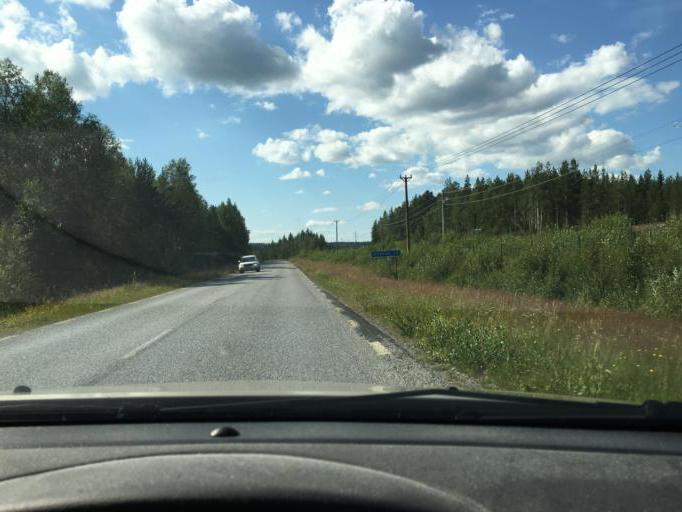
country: SE
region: Norrbotten
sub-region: Kalix Kommun
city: Toere
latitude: 66.0533
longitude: 22.5733
